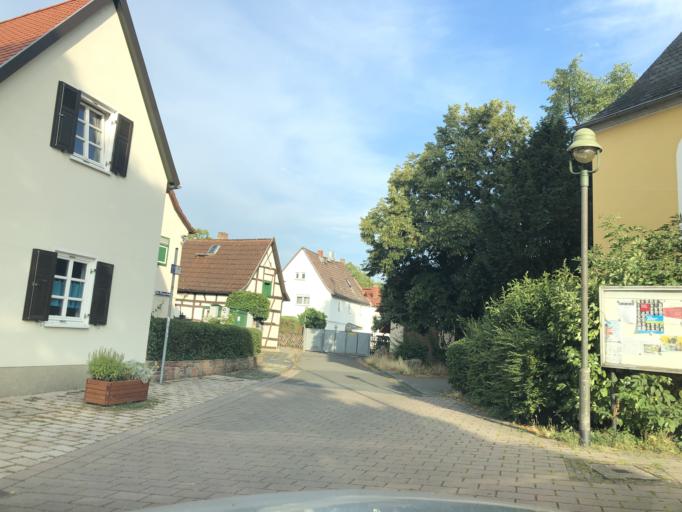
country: DE
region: Hesse
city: Raunheim
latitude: 49.9848
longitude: 8.4567
